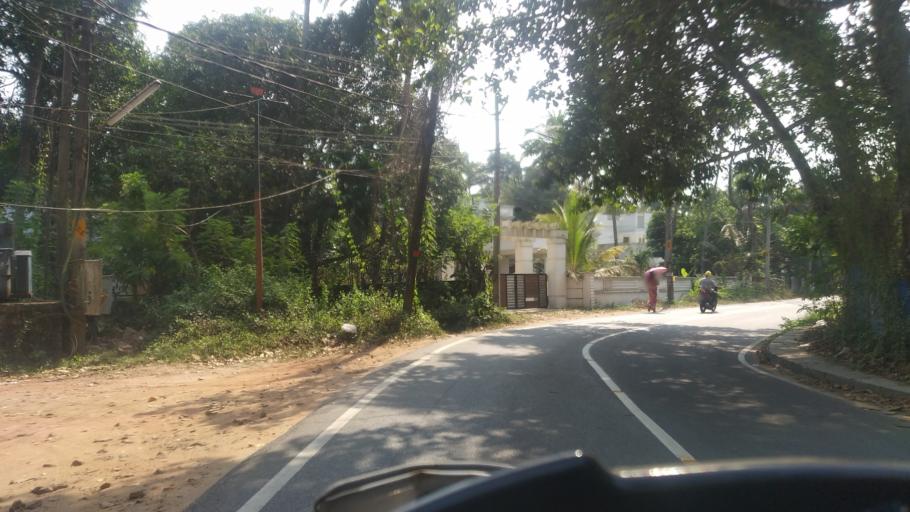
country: IN
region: Kerala
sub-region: Thrissur District
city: Kodungallur
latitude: 10.2106
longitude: 76.1878
